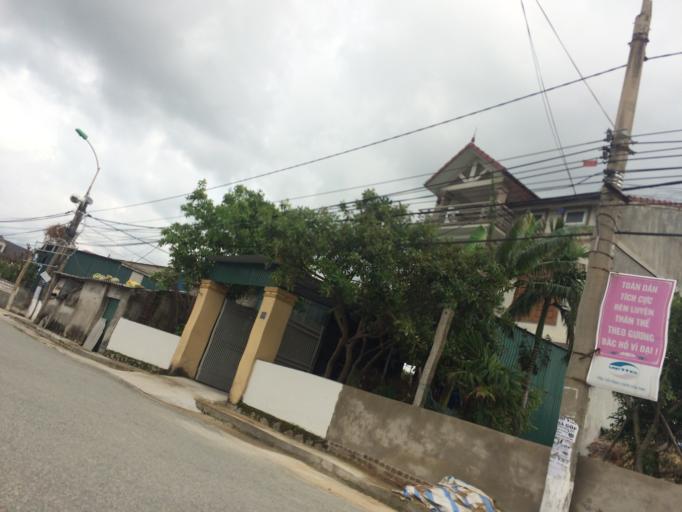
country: VN
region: Ha Tinh
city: Ha Tinh
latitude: 18.3326
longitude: 105.9213
